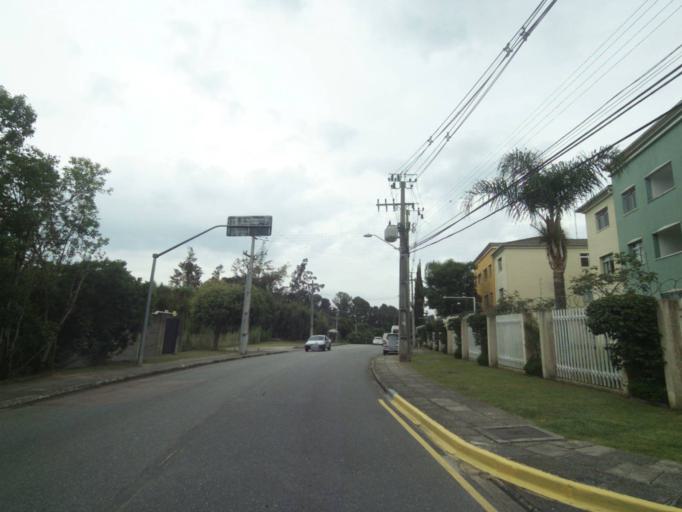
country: BR
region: Parana
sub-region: Curitiba
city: Curitiba
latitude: -25.4088
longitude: -49.3040
